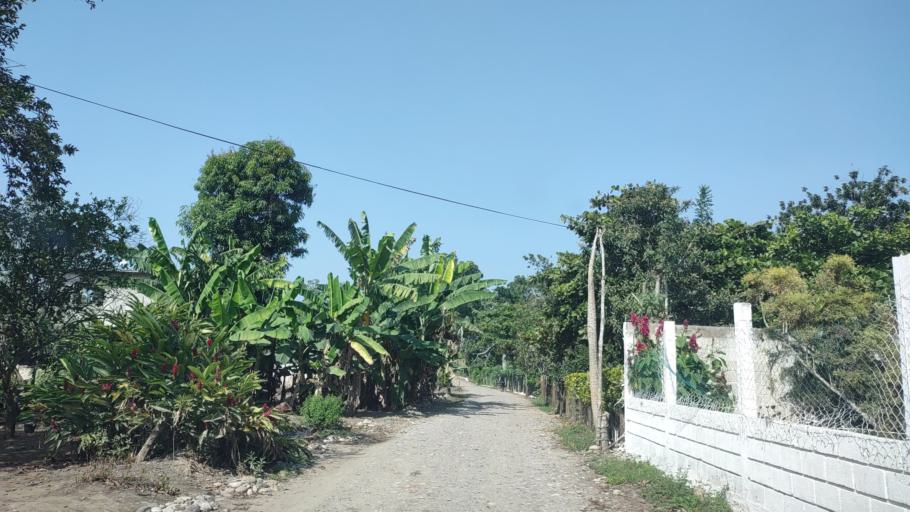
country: MX
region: Veracruz
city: Agua Dulce
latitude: 20.2774
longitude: -97.2858
